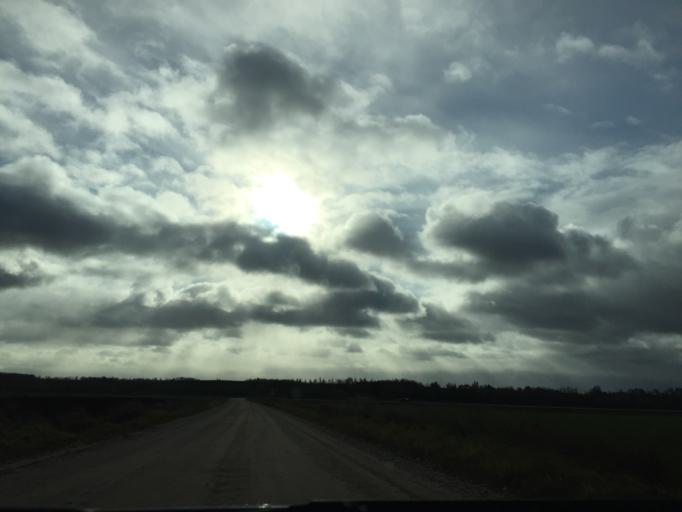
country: LV
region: Tukuma Rajons
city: Tukums
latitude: 56.9692
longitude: 23.0673
